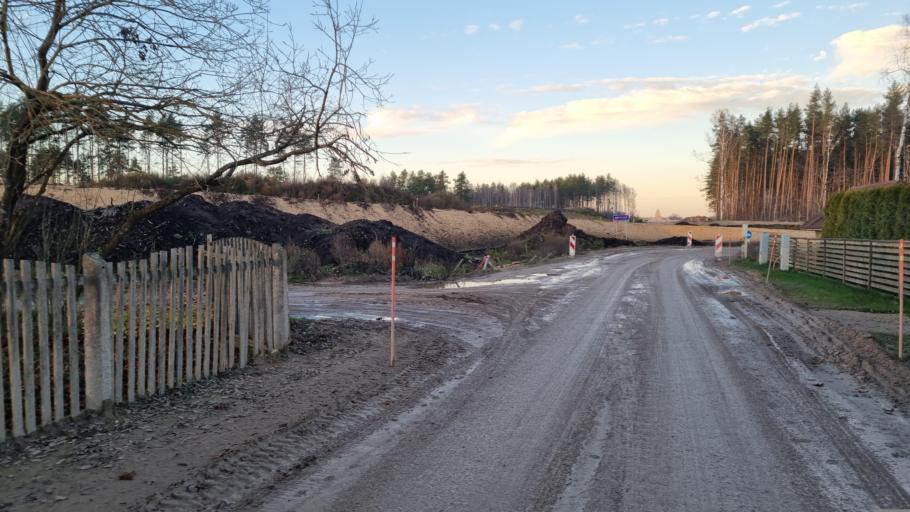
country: LV
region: Kekava
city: Balozi
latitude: 56.8657
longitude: 24.1659
